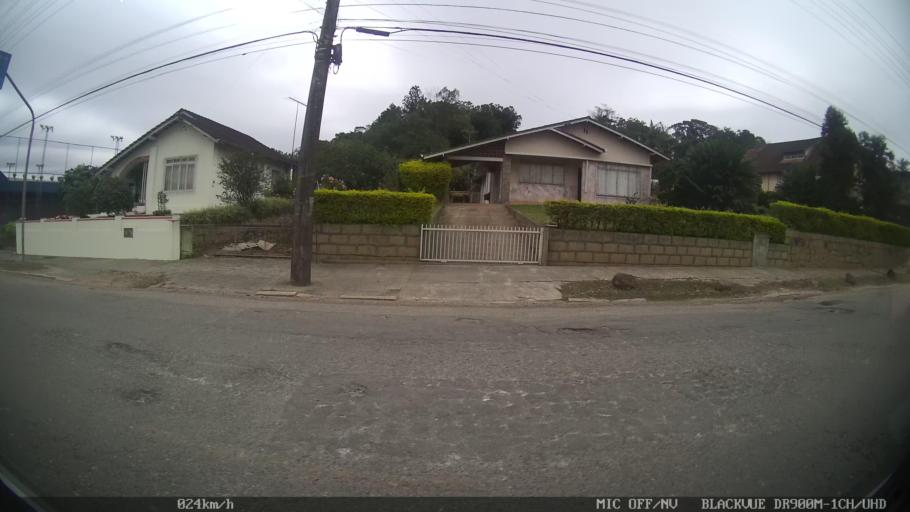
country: BR
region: Santa Catarina
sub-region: Joinville
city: Joinville
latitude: -26.2610
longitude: -48.8650
